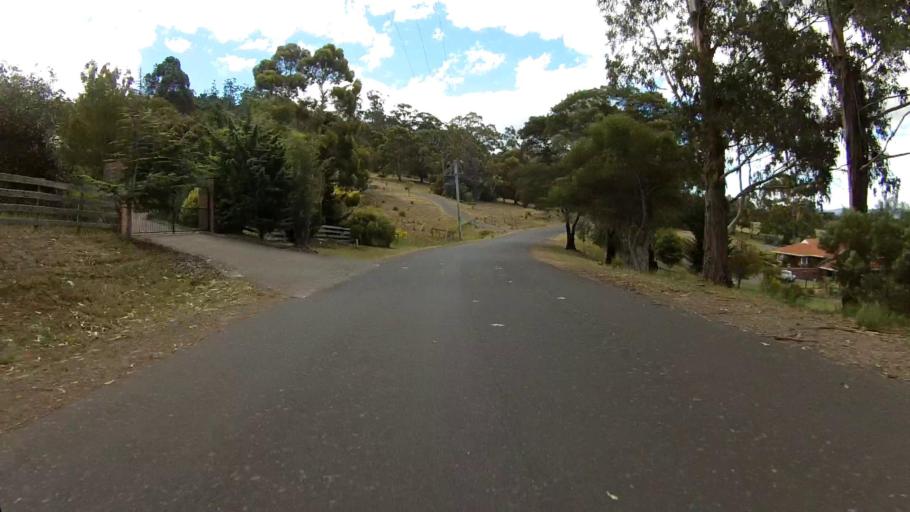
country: AU
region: Tasmania
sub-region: Clarence
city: Acton Park
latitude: -42.8838
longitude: 147.4713
